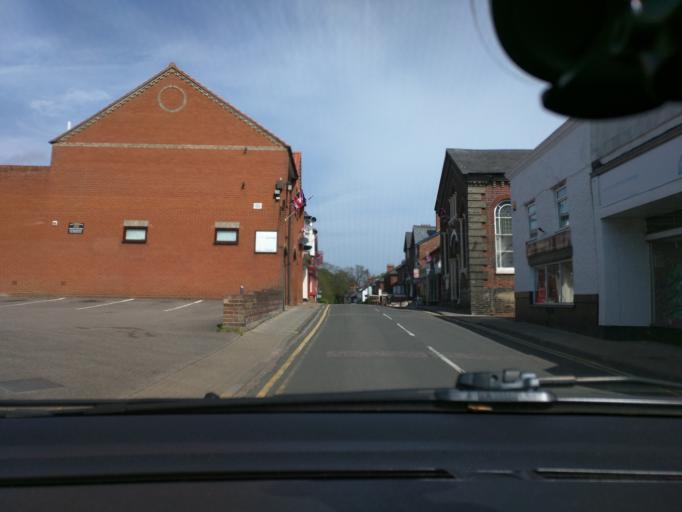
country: GB
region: England
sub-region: Suffolk
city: Leiston
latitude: 52.2063
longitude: 1.5775
